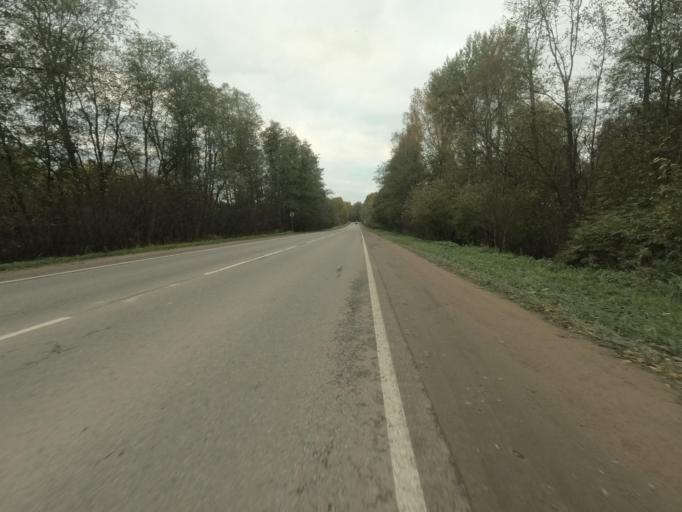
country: RU
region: Leningrad
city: Pavlovo
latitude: 59.7951
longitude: 30.9517
